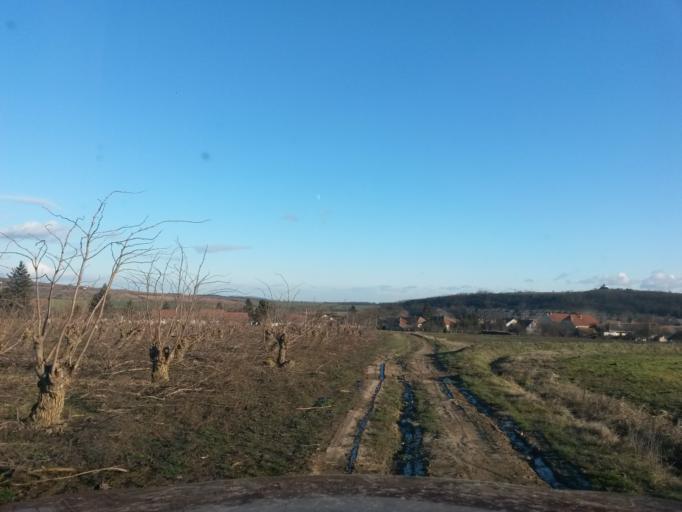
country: HU
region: Borsod-Abauj-Zemplen
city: Sarospatak
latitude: 48.3327
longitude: 21.5279
